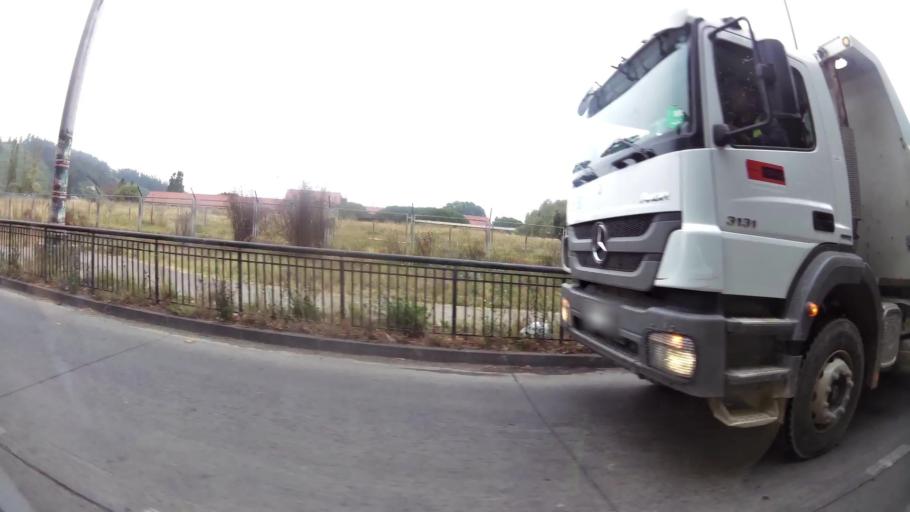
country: CL
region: Biobio
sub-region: Provincia de Concepcion
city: Concepcion
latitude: -36.8129
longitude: -73.0290
